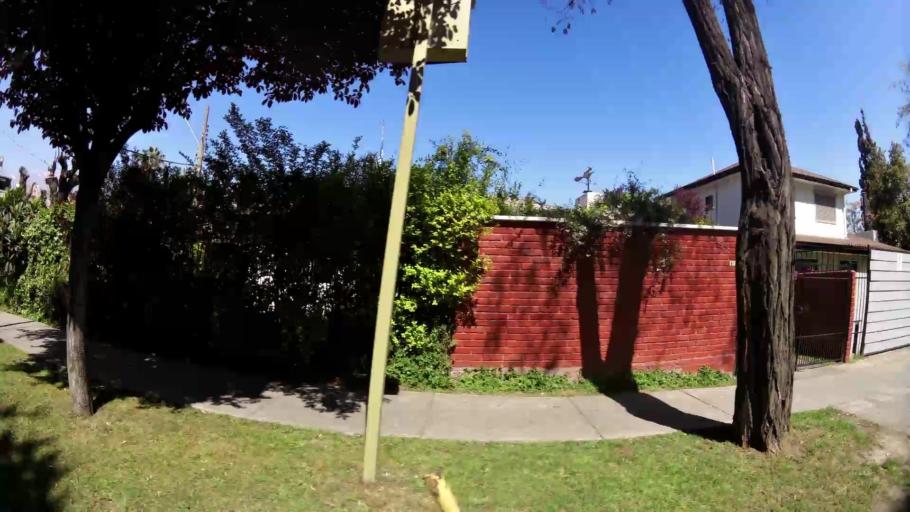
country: CL
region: Santiago Metropolitan
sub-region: Provincia de Santiago
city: Villa Presidente Frei, Nunoa, Santiago, Chile
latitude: -33.4210
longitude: -70.5724
